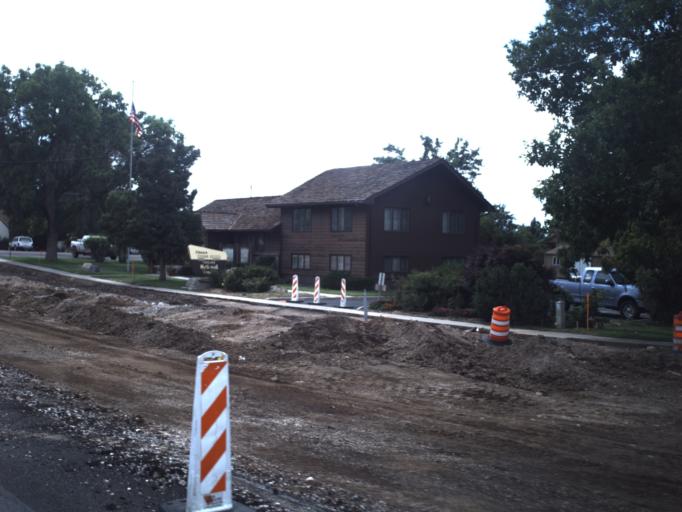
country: US
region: Utah
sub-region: Millard County
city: Fillmore
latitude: 38.9610
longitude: -112.3236
